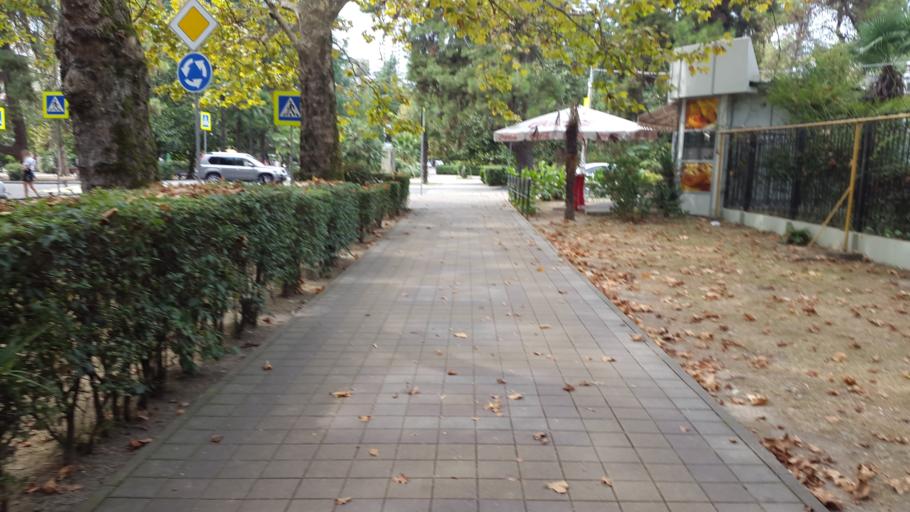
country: RU
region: Krasnodarskiy
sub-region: Sochi City
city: Sochi
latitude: 43.6015
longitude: 39.7262
